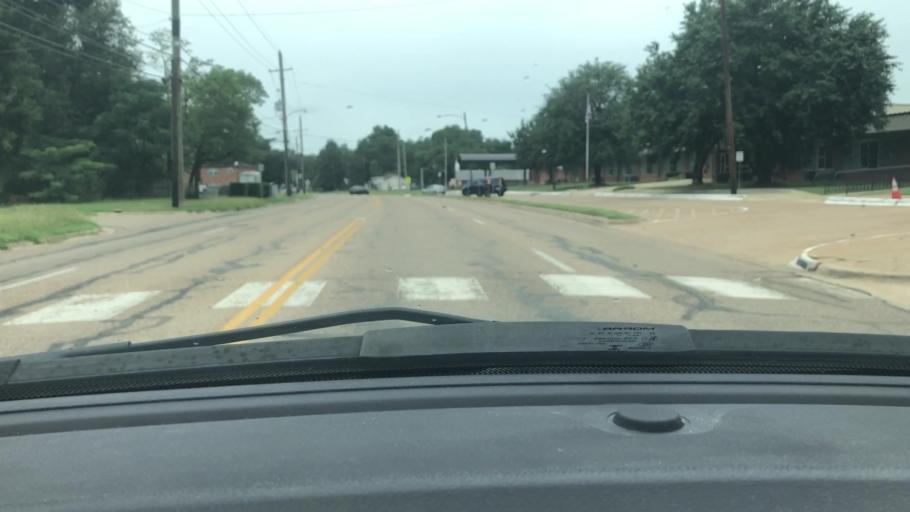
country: US
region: Texas
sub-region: Bowie County
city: Wake Village
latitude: 33.4364
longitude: -94.0850
